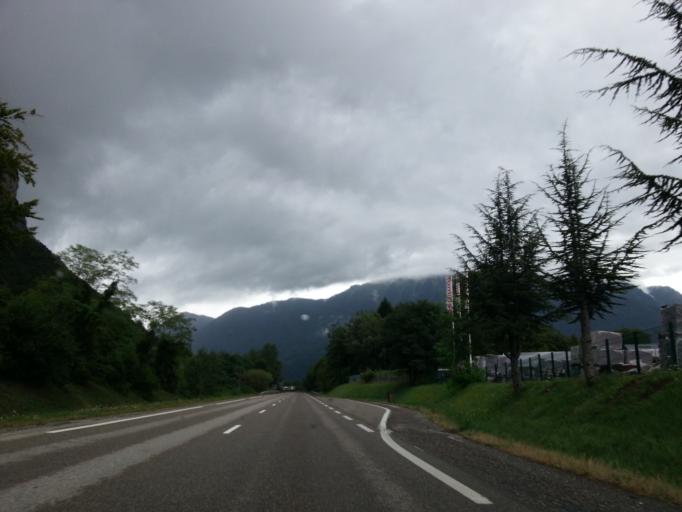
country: FR
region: Rhone-Alpes
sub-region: Departement de la Haute-Savoie
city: Faverges
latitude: 45.7555
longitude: 6.2775
